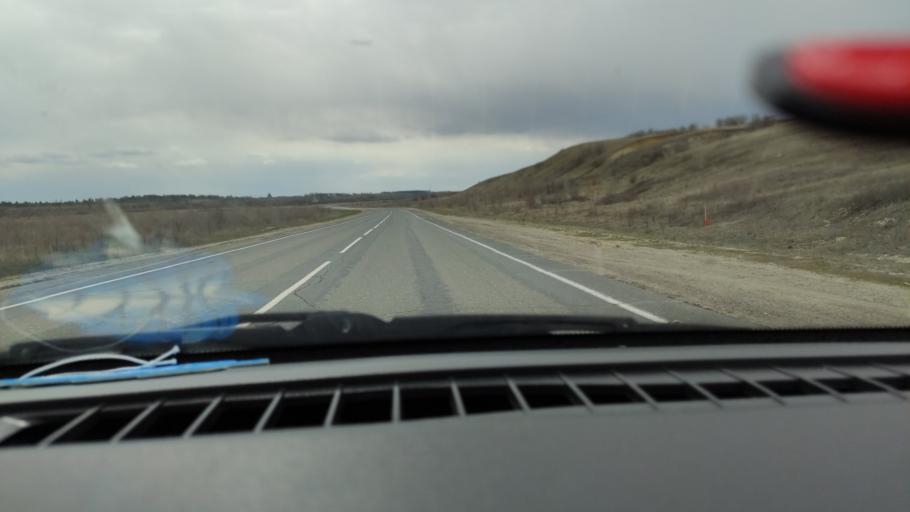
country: RU
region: Saratov
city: Sennoy
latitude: 52.0945
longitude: 46.8118
